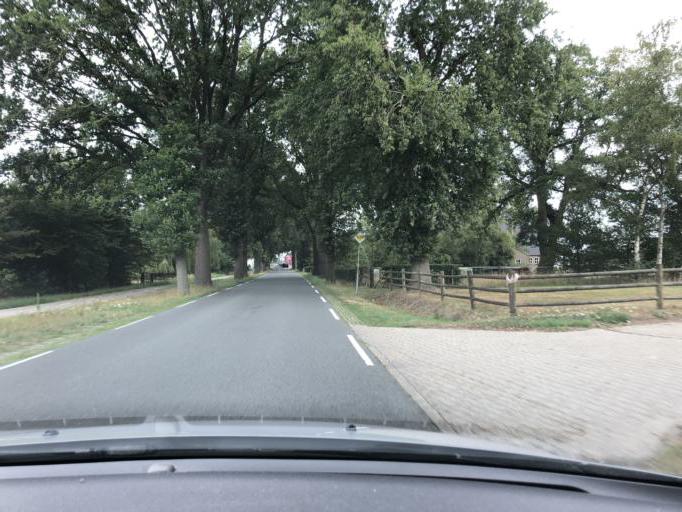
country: NL
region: Drenthe
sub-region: Gemeente Assen
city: Assen
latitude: 52.8823
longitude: 6.6482
